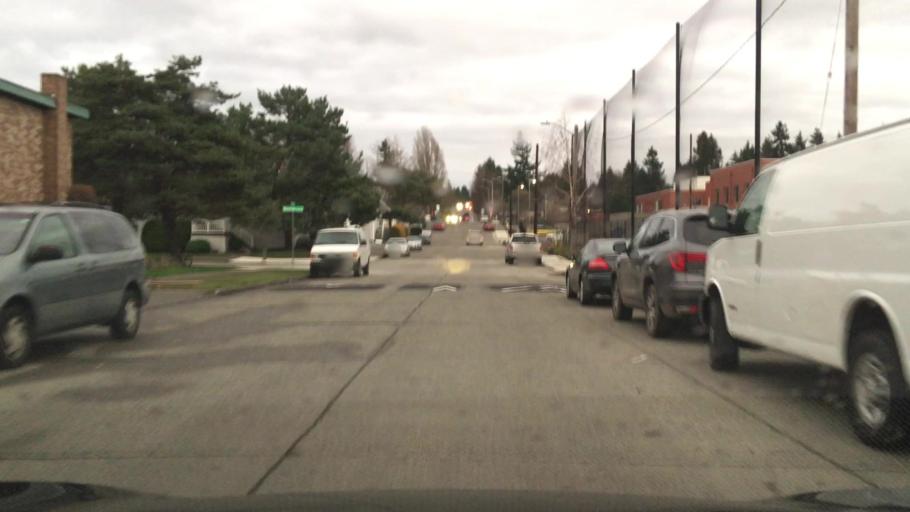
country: US
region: Washington
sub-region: King County
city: Shoreline
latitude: 47.6960
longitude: -122.3394
